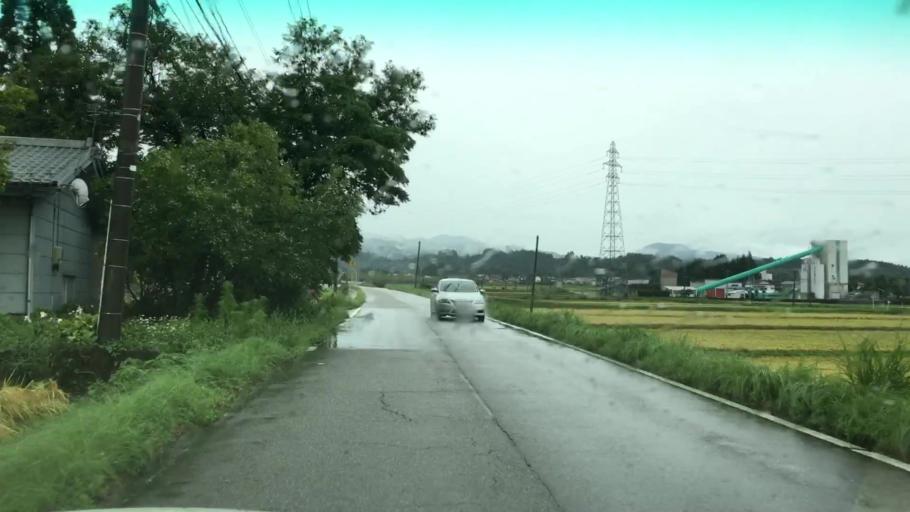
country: JP
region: Toyama
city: Kamiichi
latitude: 36.6182
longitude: 137.3223
